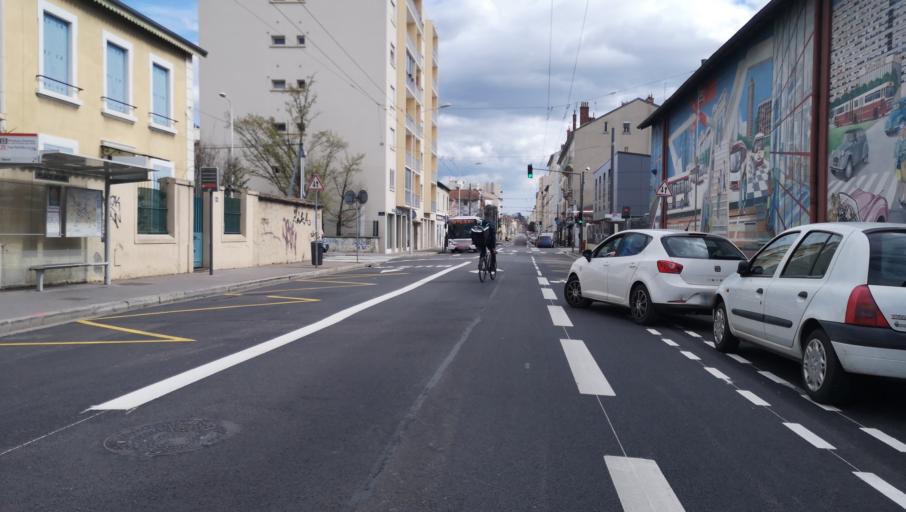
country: FR
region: Rhone-Alpes
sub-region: Departement du Rhone
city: Villeurbanne
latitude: 45.7485
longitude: 4.8791
